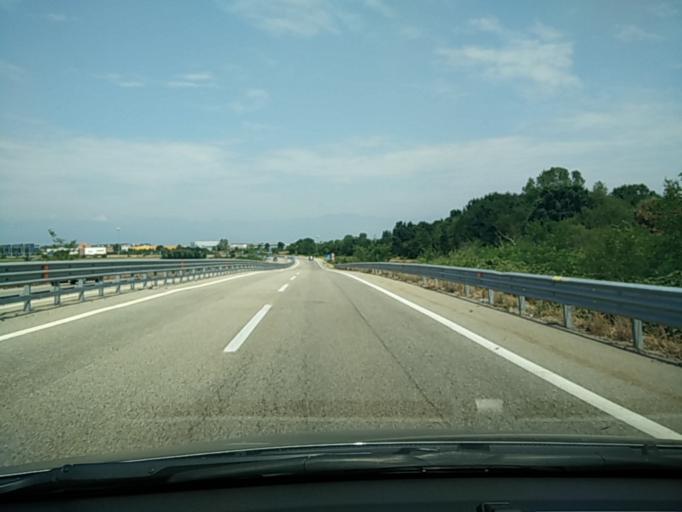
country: IT
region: Piedmont
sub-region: Provincia di Torino
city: Volpiano
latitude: 45.1797
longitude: 7.8012
